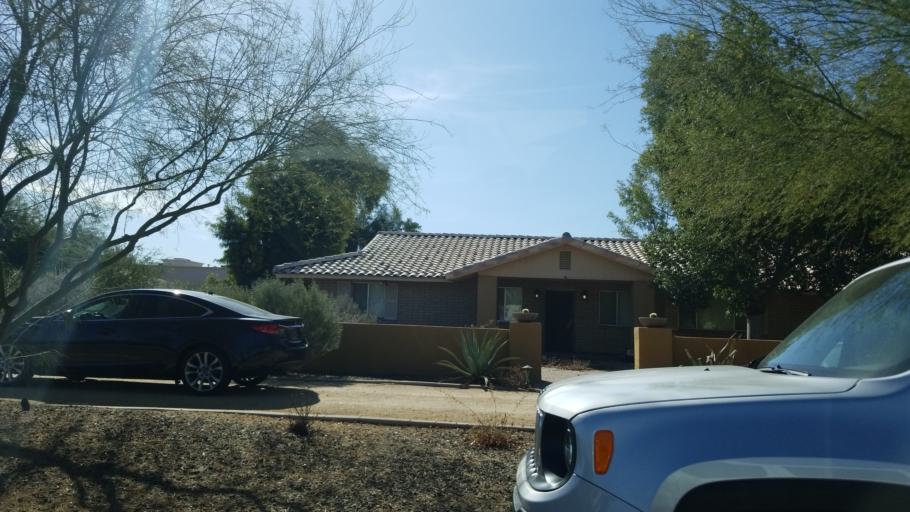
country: US
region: Arizona
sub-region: Maricopa County
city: Paradise Valley
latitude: 33.5863
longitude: -111.9798
